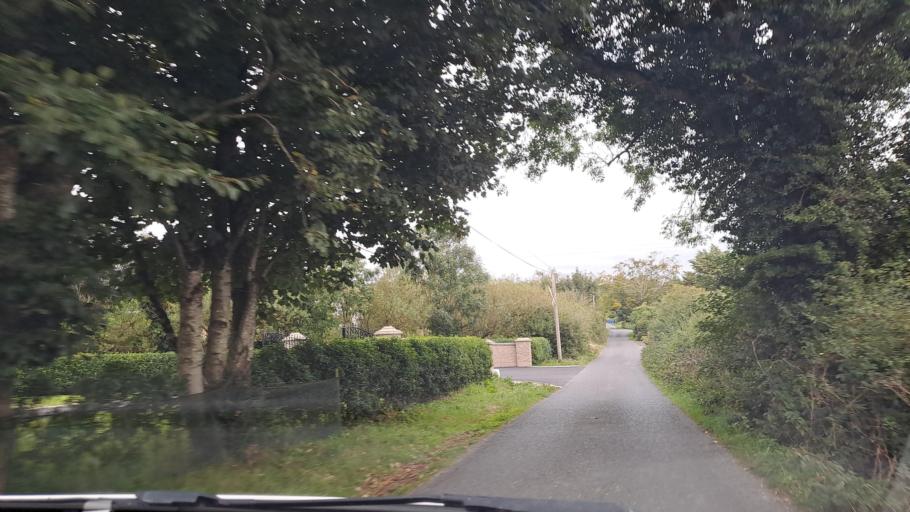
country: IE
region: Ulster
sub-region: County Monaghan
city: Carrickmacross
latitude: 54.0332
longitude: -6.7799
